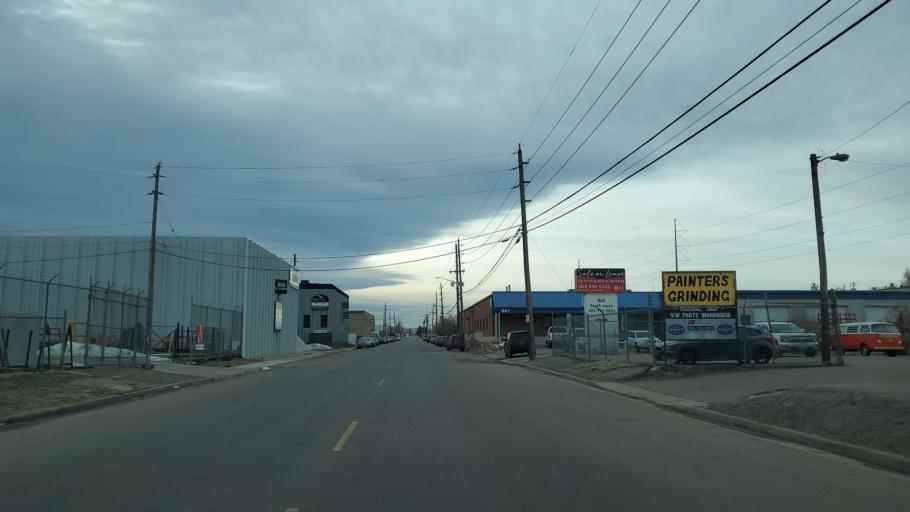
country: US
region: Colorado
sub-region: Denver County
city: Denver
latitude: 39.7017
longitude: -104.9992
